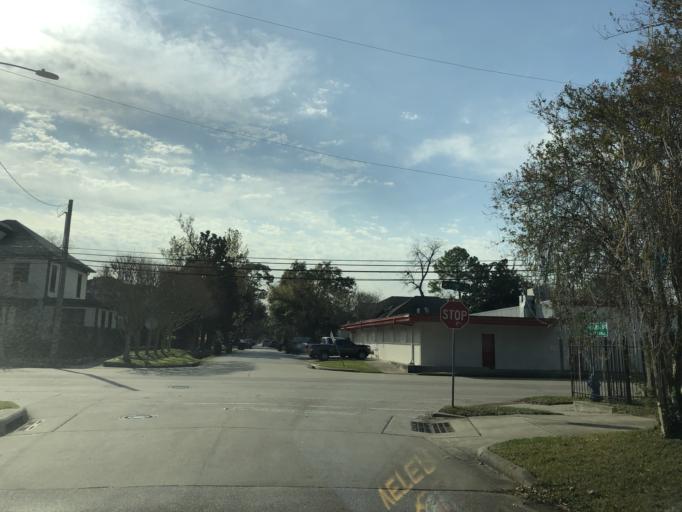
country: US
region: Texas
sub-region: Harris County
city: Houston
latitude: 29.7912
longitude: -95.3943
